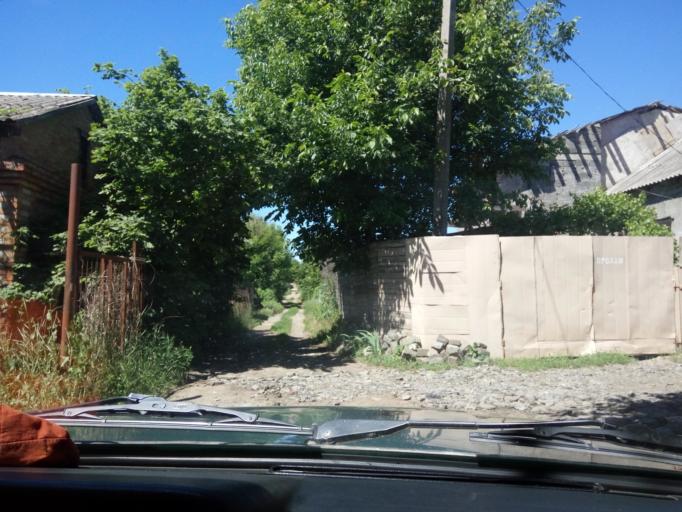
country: RU
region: Rostov
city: Bataysk
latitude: 47.0782
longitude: 39.7509
